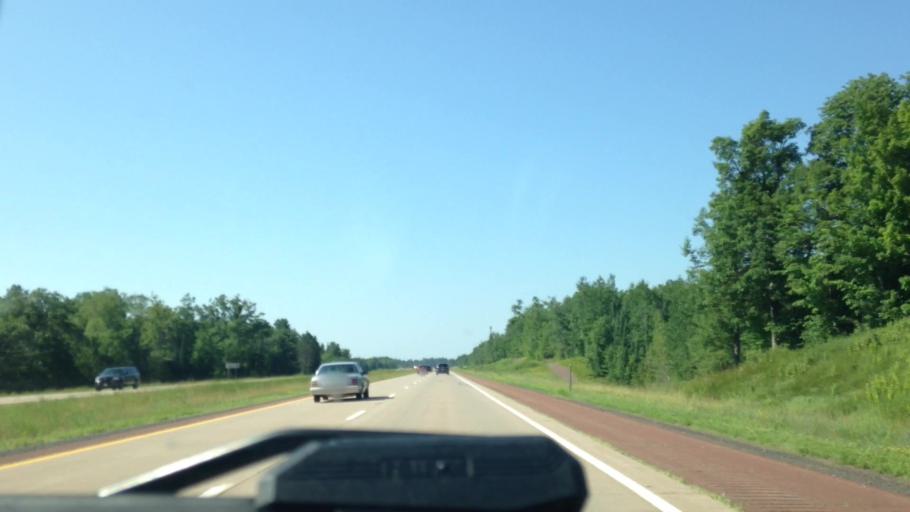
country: US
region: Wisconsin
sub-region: Douglas County
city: Lake Nebagamon
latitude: 46.3732
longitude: -91.8267
